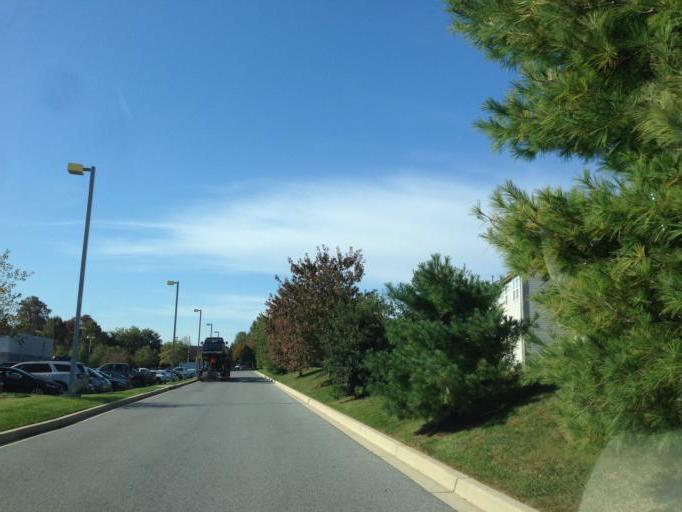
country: US
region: Maryland
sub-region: Howard County
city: Ellicott City
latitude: 39.2831
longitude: -76.8129
